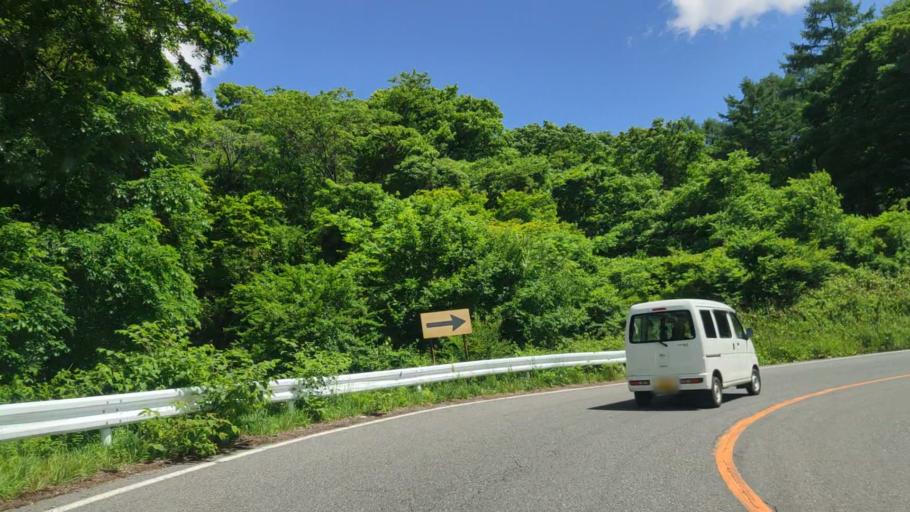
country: JP
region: Nagano
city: Chino
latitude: 36.0828
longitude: 138.2211
